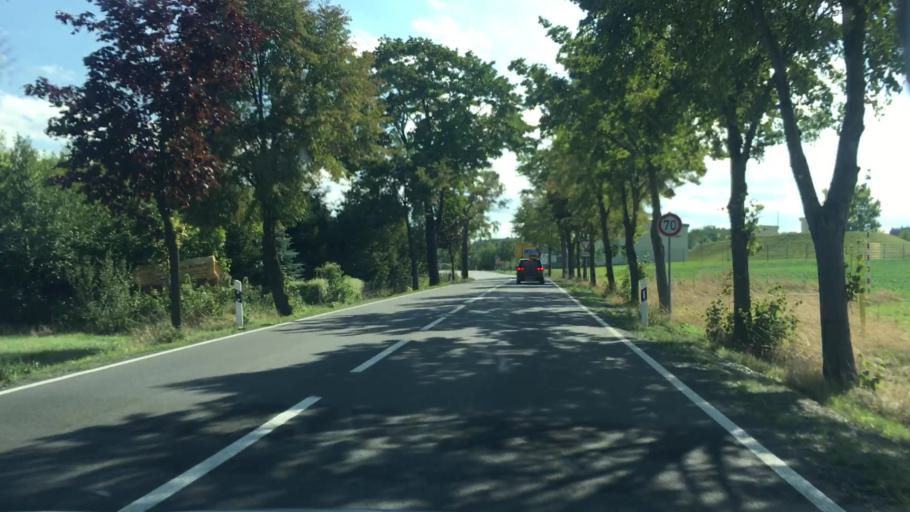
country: DE
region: Saxony
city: Dohma
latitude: 50.9012
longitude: 13.9457
